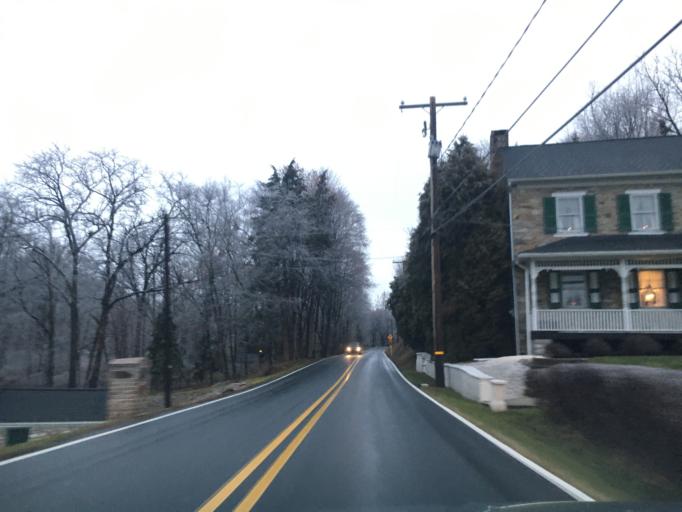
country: US
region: Pennsylvania
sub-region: Lehigh County
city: Schnecksville
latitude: 40.6371
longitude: -75.5981
